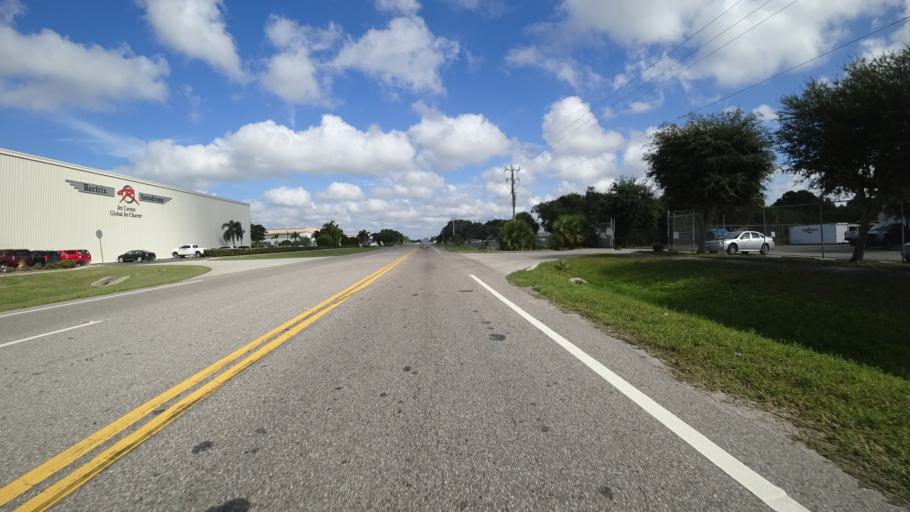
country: US
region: Florida
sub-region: Manatee County
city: Whitfield
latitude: 27.3933
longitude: -82.5468
